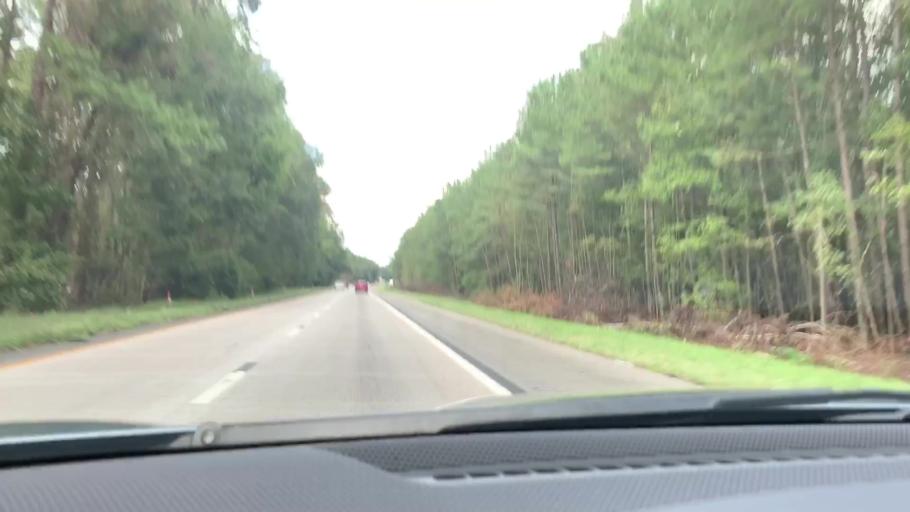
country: US
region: South Carolina
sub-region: Jasper County
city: Ridgeland
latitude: 32.4125
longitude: -81.0130
